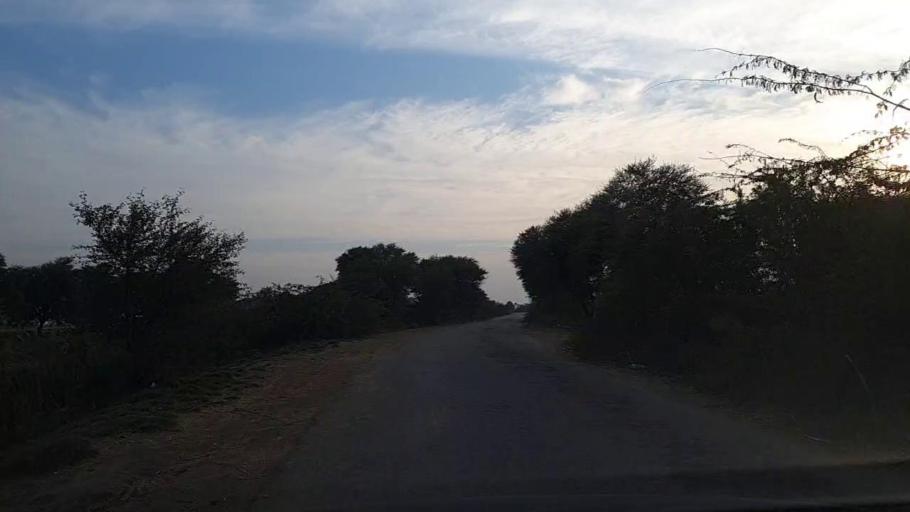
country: PK
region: Sindh
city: Nawabshah
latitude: 26.4014
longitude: 68.4815
